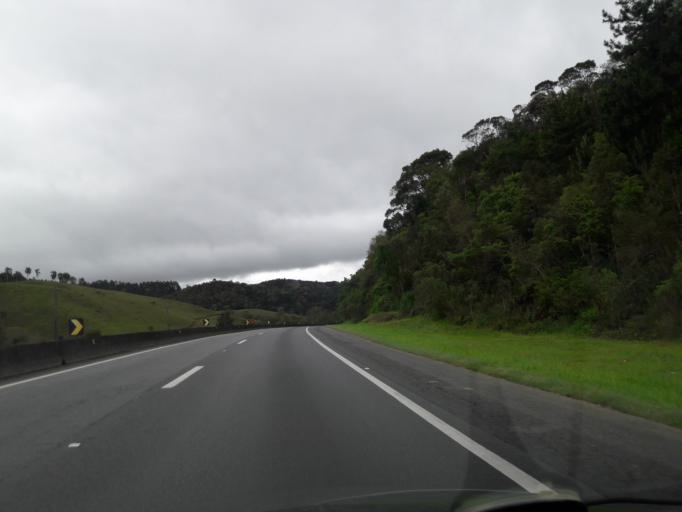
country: BR
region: Parana
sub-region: Campina Grande Do Sul
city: Campina Grande do Sul
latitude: -25.2368
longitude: -48.9072
